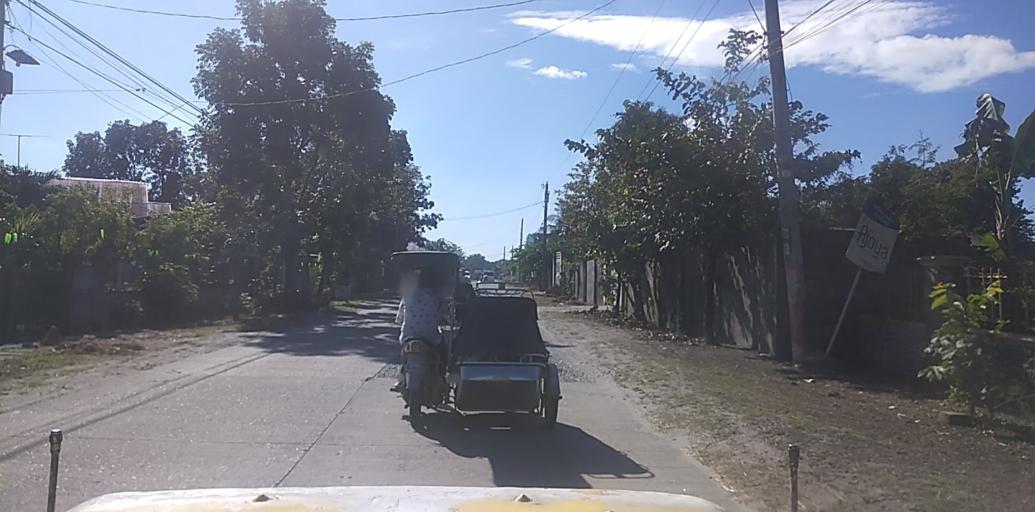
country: PH
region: Central Luzon
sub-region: Province of Pampanga
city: Mexico
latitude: 15.0806
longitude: 120.7170
